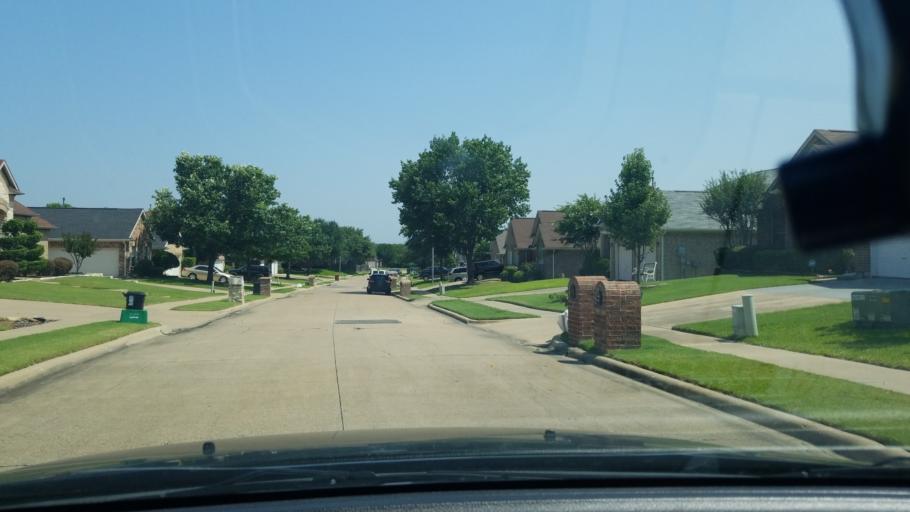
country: US
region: Texas
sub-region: Dallas County
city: Sunnyvale
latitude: 32.8260
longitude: -96.6002
